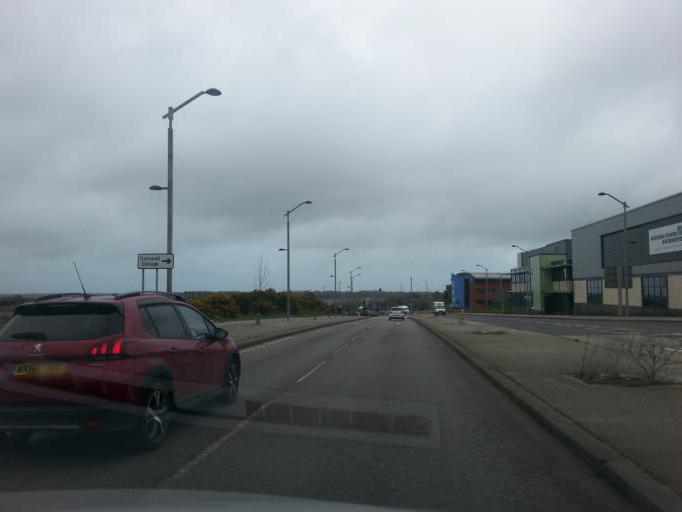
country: GB
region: England
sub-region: Cornwall
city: Camborne
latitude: 50.2255
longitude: -5.2780
